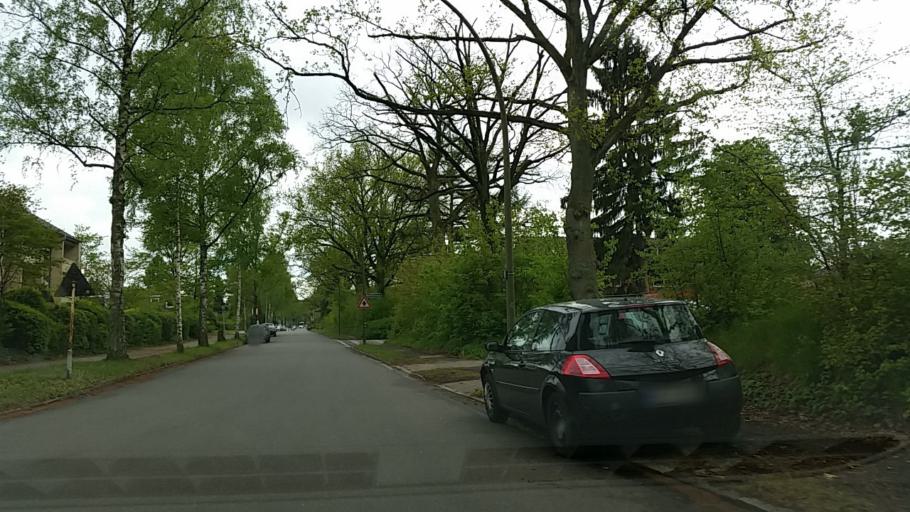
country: DE
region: Hamburg
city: Sasel
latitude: 53.6626
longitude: 10.1068
